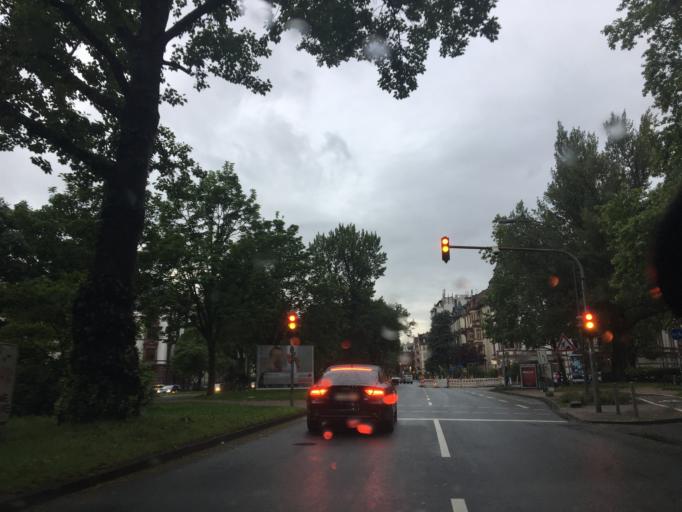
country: DE
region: Hesse
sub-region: Regierungsbezirk Darmstadt
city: Frankfurt am Main
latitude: 50.1264
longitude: 8.6980
